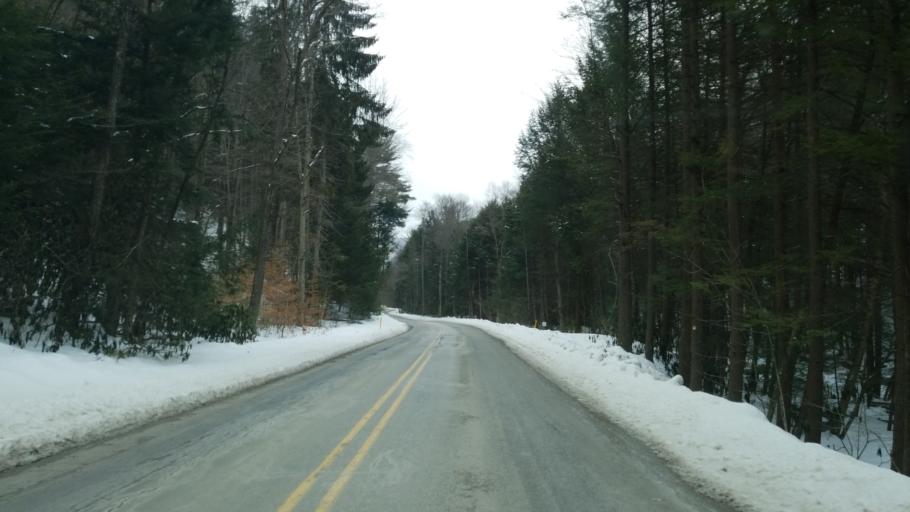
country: US
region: Pennsylvania
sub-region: Clearfield County
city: Shiloh
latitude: 41.2505
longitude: -78.1518
